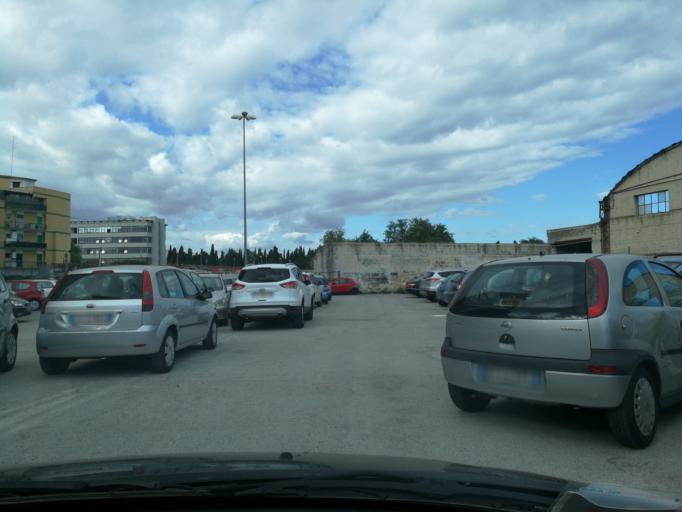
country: IT
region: Apulia
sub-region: Provincia di Bari
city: Bari
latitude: 41.1234
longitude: 16.8509
